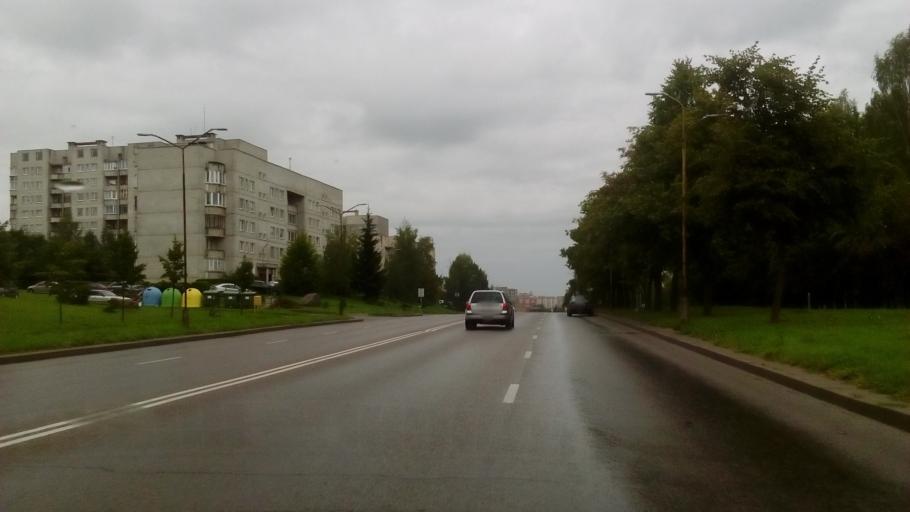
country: LT
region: Alytaus apskritis
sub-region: Alytus
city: Alytus
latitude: 54.3897
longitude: 24.0233
